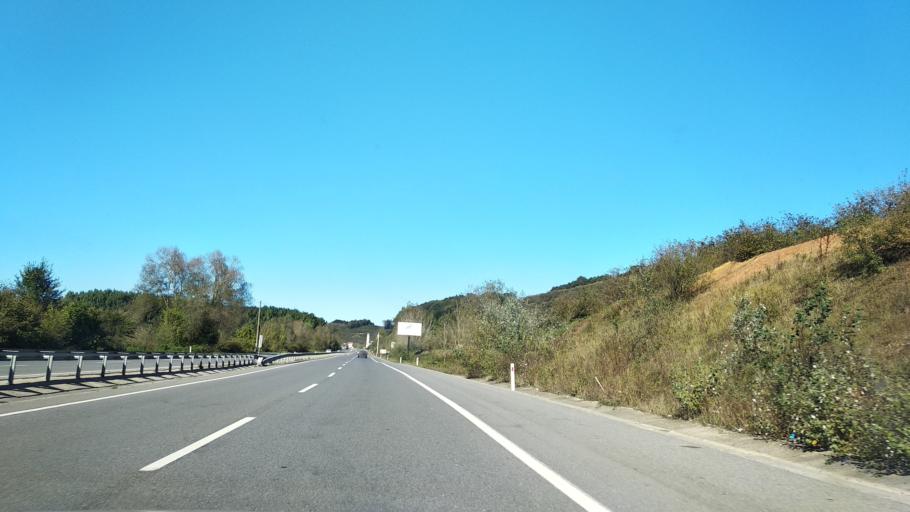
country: TR
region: Sakarya
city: Karasu
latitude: 41.0673
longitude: 30.6435
